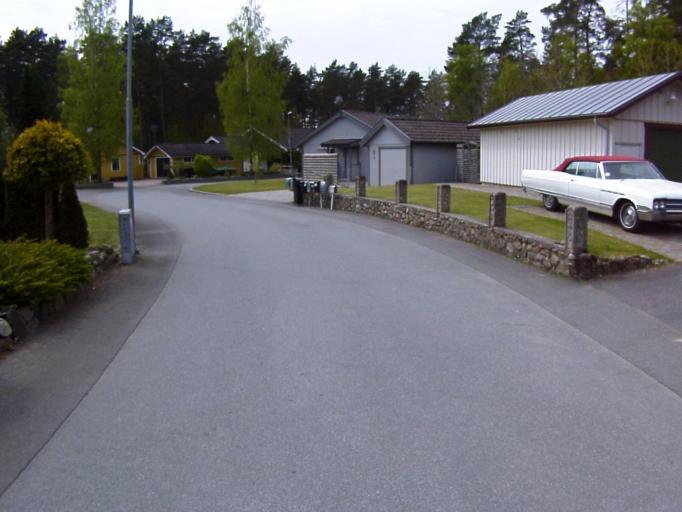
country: SE
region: Skane
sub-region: Kristianstads Kommun
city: Fjalkinge
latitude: 56.0478
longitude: 14.3317
